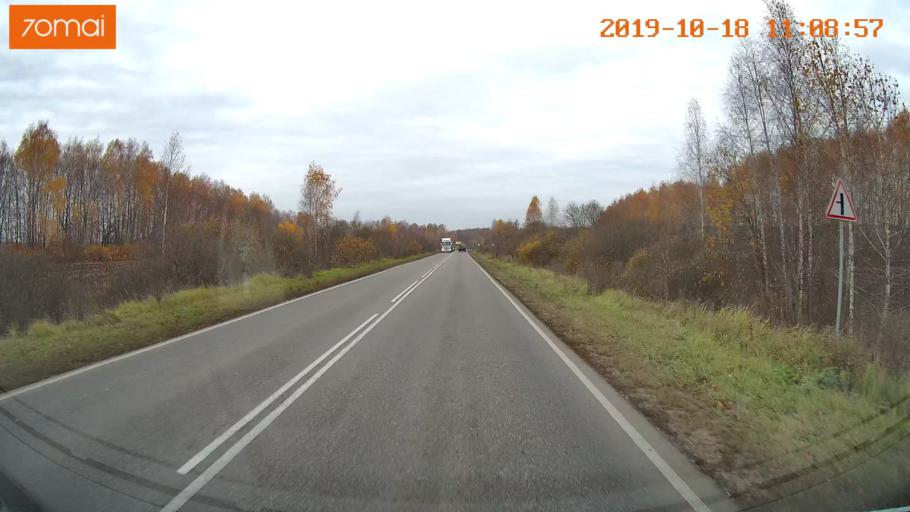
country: RU
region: Tula
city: Kimovsk
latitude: 53.9461
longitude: 38.5338
